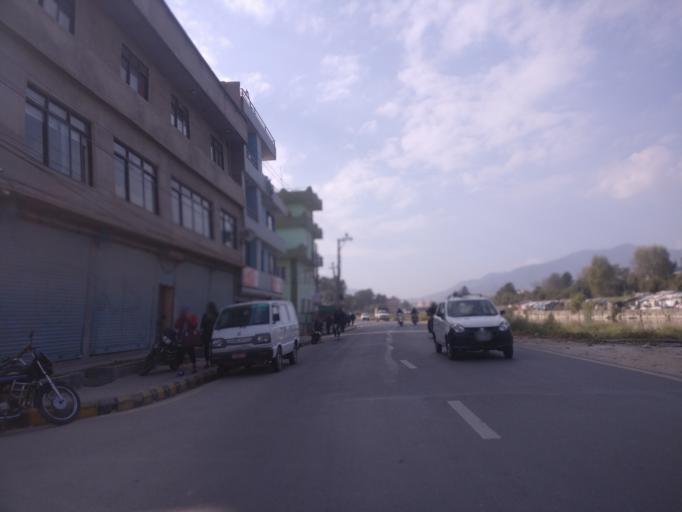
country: NP
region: Central Region
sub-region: Bagmati Zone
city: Patan
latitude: 27.6866
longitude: 85.3211
